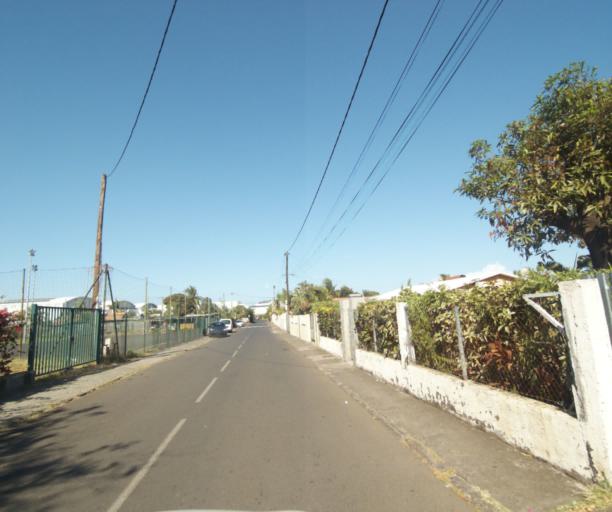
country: RE
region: Reunion
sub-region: Reunion
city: Saint-Paul
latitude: -20.9856
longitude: 55.2940
